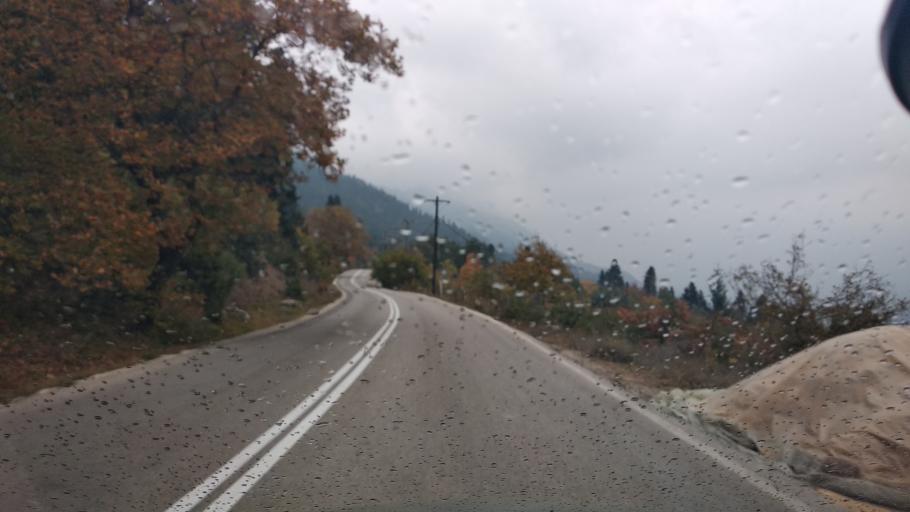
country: GR
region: Thessaly
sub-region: Trikala
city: Pyli
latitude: 39.5150
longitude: 21.5268
